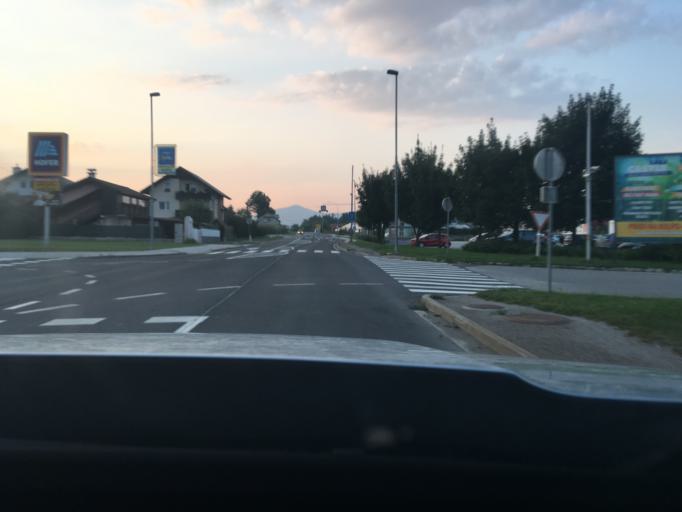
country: SI
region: Kocevje
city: Kocevje
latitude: 45.6497
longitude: 14.8537
